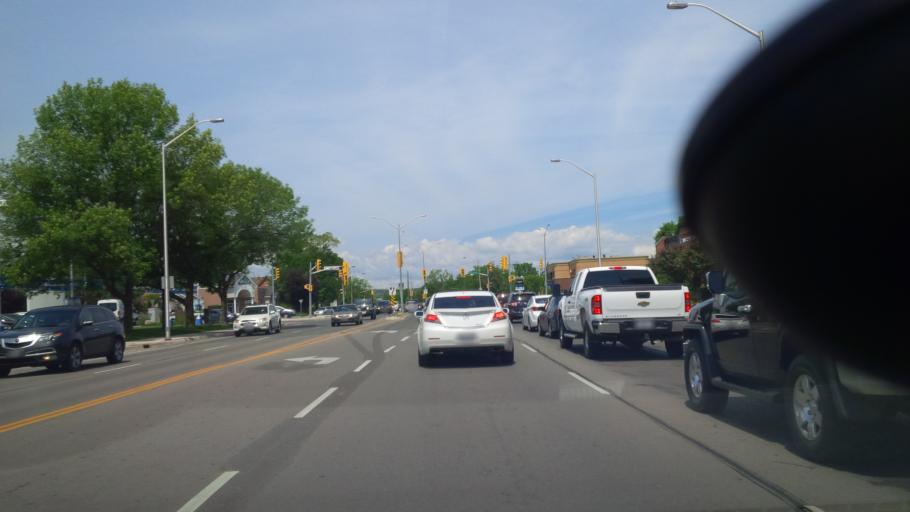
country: CA
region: Ontario
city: Burlington
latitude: 43.3352
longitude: -79.8117
